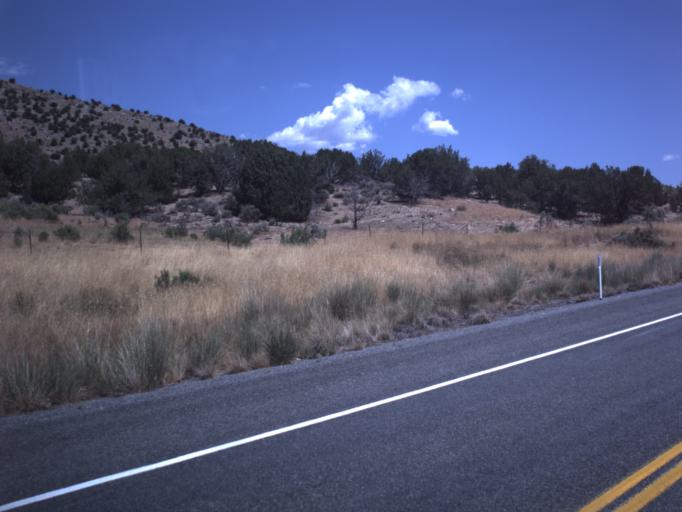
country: US
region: Utah
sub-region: Juab County
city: Nephi
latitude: 39.5923
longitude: -112.1560
